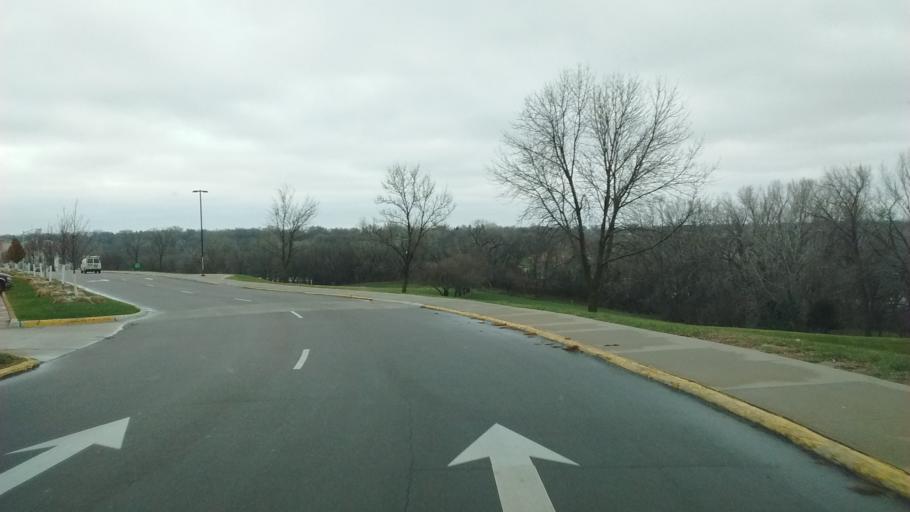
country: US
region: Iowa
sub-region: Woodbury County
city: Sioux City
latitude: 42.4835
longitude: -96.3507
